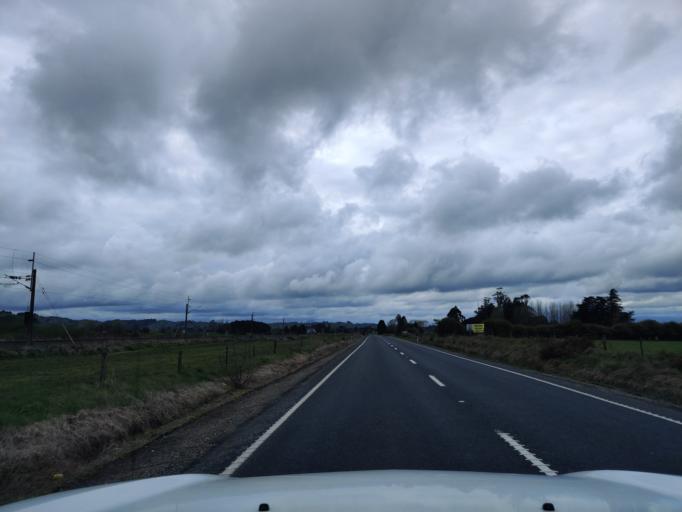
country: NZ
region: Waikato
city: Turangi
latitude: -39.0207
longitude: 175.3795
